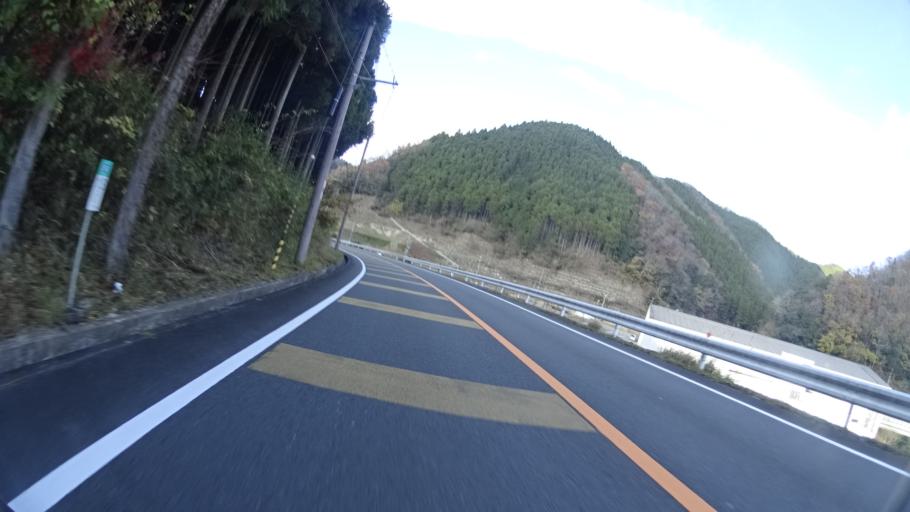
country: JP
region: Kyoto
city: Kameoka
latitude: 35.1521
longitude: 135.5156
